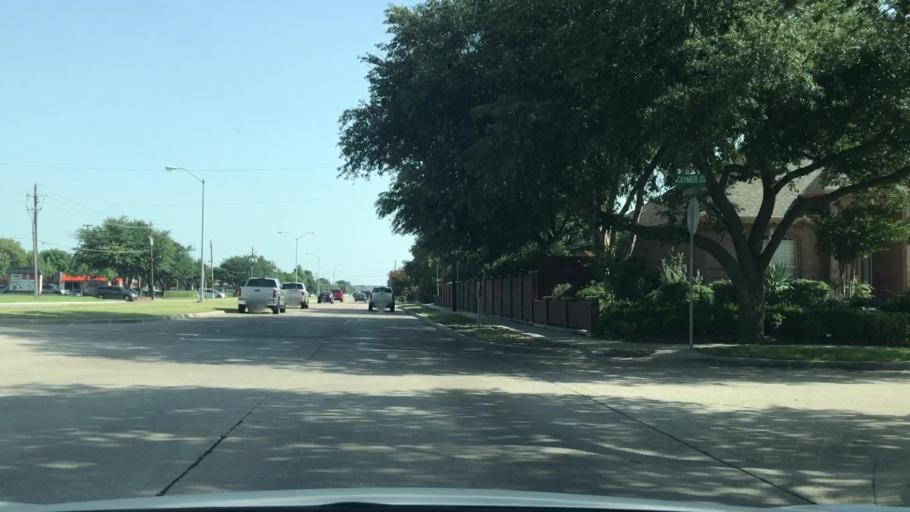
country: US
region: Texas
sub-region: Collin County
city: Plano
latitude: 33.0759
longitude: -96.7504
